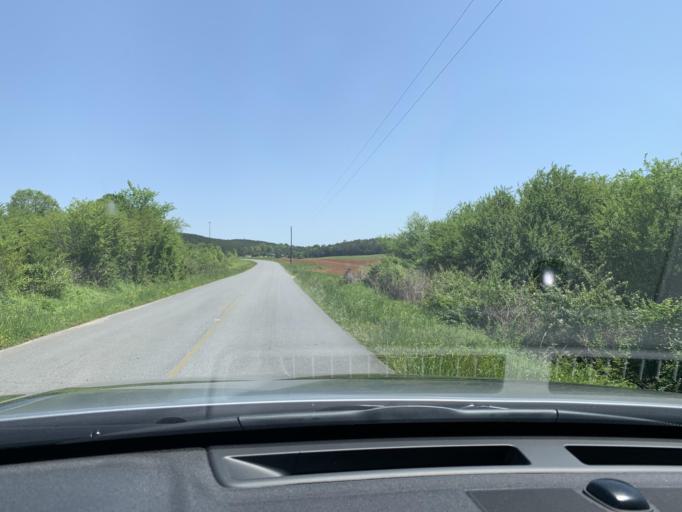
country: US
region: Georgia
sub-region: Polk County
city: Cedartown
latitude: 34.0639
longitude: -85.1715
